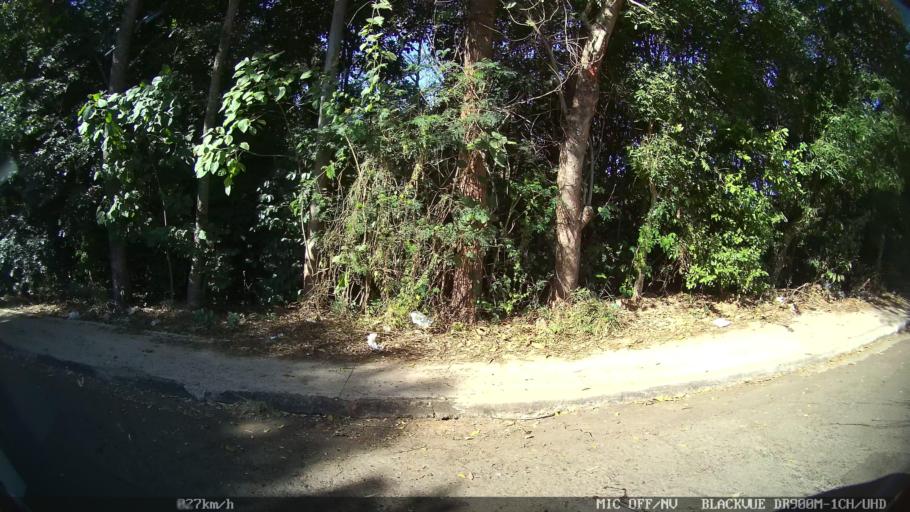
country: BR
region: Sao Paulo
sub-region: Franca
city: Franca
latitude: -20.4930
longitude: -47.4138
